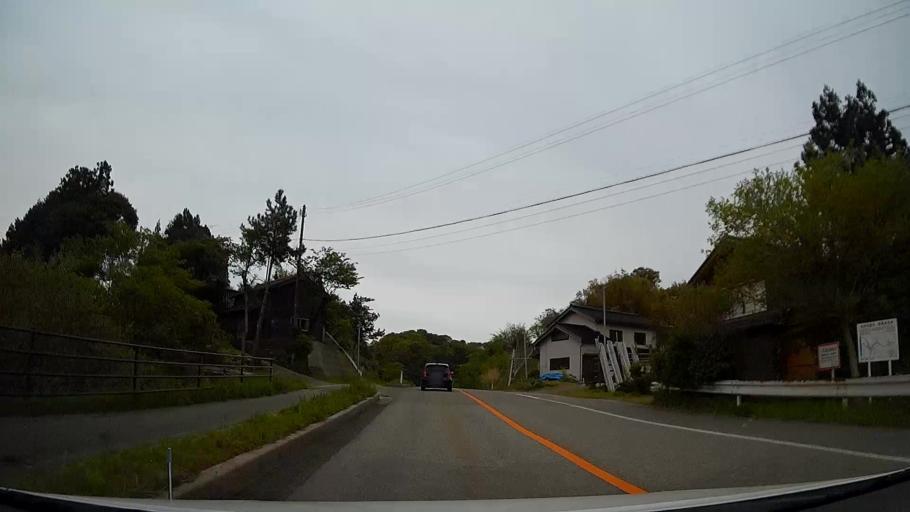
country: JP
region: Ishikawa
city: Nanao
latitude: 37.4062
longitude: 136.9589
